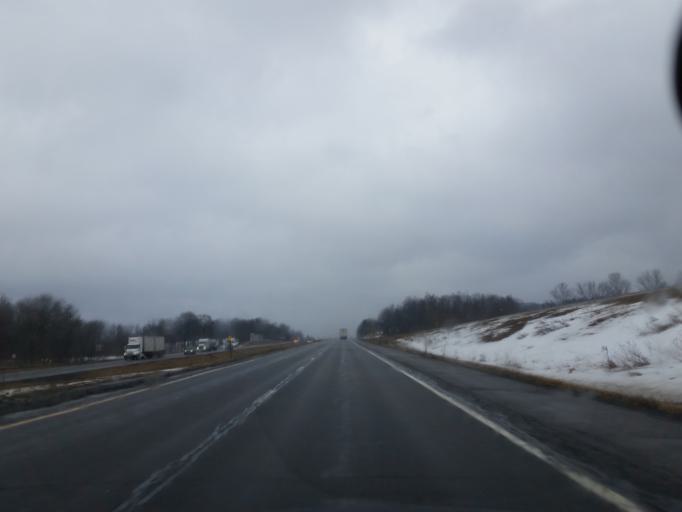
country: US
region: New York
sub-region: Chenango County
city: Lakeview
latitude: 42.3208
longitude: -75.9711
